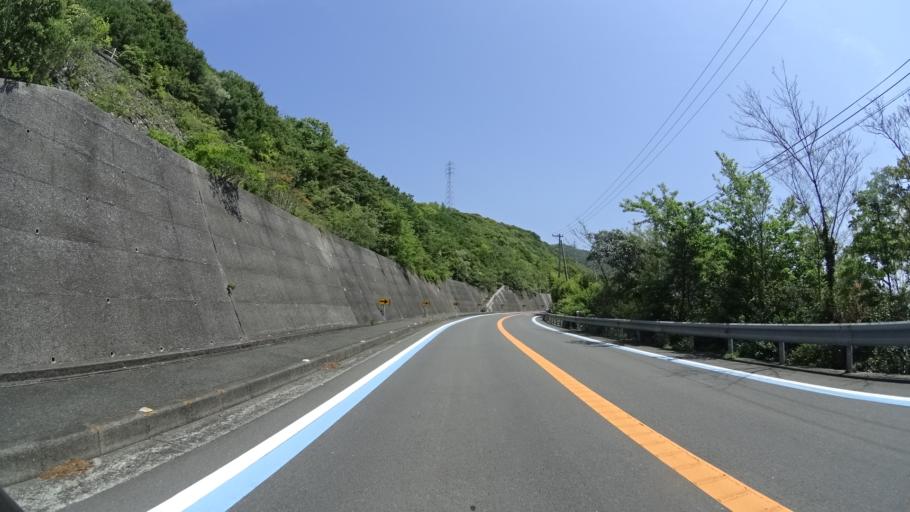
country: JP
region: Ehime
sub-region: Nishiuwa-gun
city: Ikata-cho
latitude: 33.4474
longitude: 132.2667
